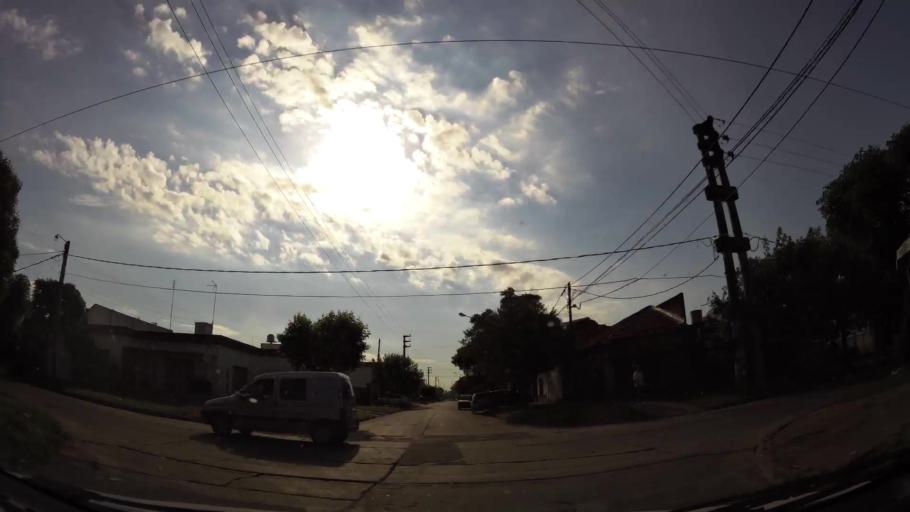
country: AR
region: Buenos Aires
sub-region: Partido de Merlo
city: Merlo
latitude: -34.6601
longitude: -58.7373
